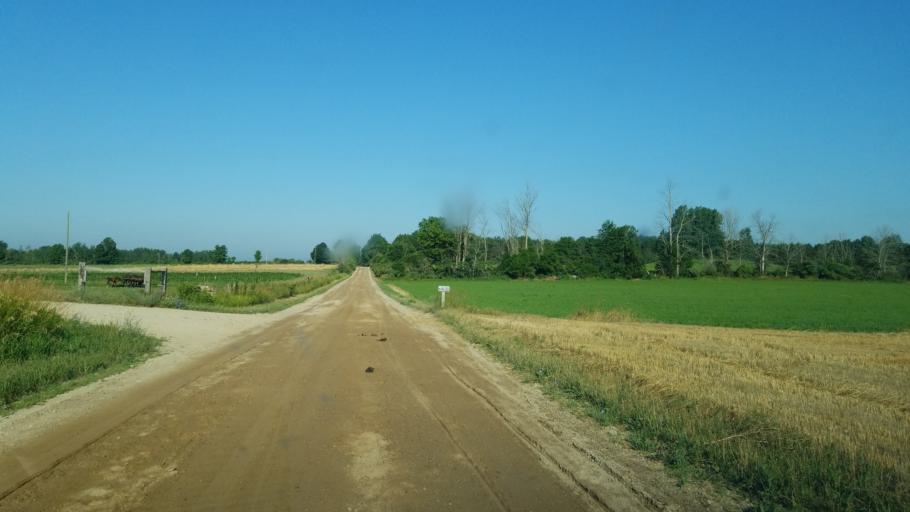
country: US
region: Michigan
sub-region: Mecosta County
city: Canadian Lakes
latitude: 43.5545
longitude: -85.3569
